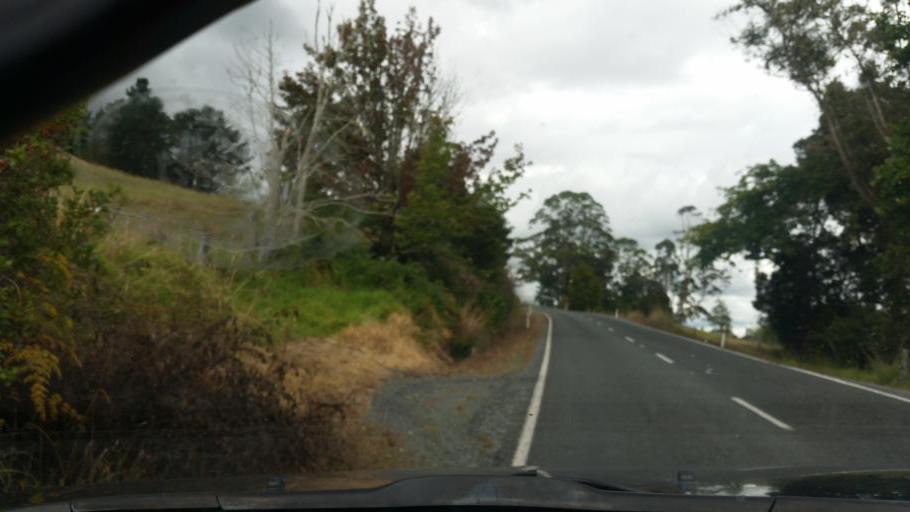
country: NZ
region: Northland
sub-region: Whangarei
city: Ruakaka
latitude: -35.9442
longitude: 174.2916
